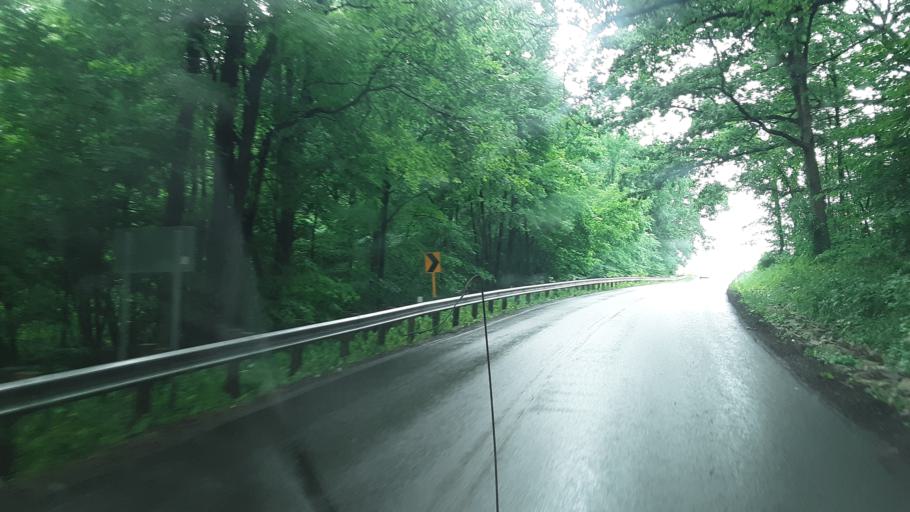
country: US
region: Ohio
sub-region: Carroll County
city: Carrollton
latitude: 40.6199
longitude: -81.0442
